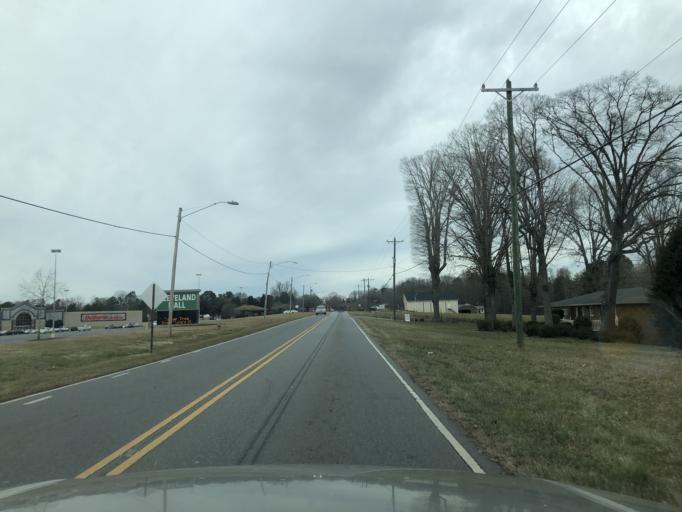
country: US
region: North Carolina
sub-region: Cleveland County
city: Shelby
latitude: 35.2680
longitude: -81.4796
